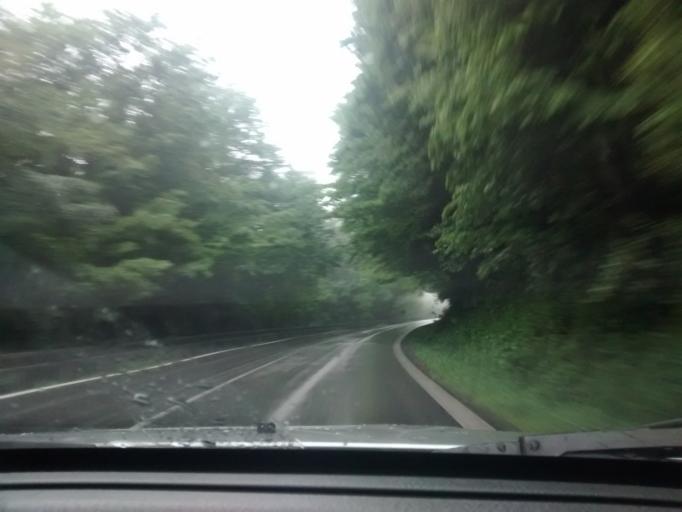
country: SK
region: Nitriansky
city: Handlova
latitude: 48.6584
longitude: 18.7342
